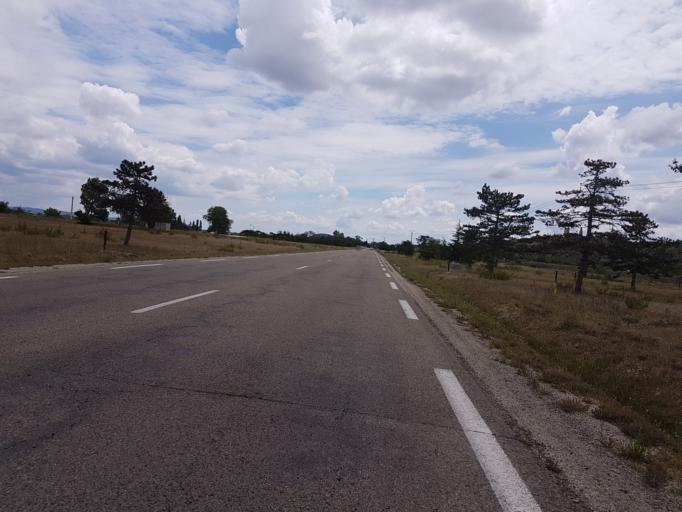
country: FR
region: Languedoc-Roussillon
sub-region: Departement du Gard
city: Vallabregues
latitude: 43.8501
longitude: 4.6184
